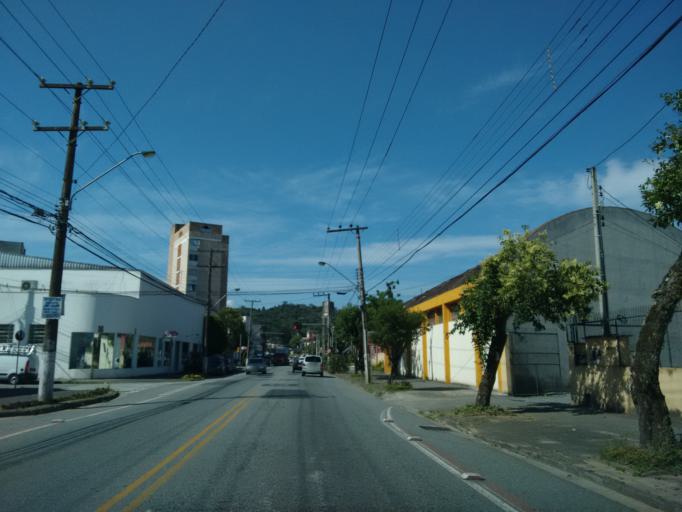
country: BR
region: Santa Catarina
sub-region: Blumenau
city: Blumenau
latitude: -26.9299
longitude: -49.0588
